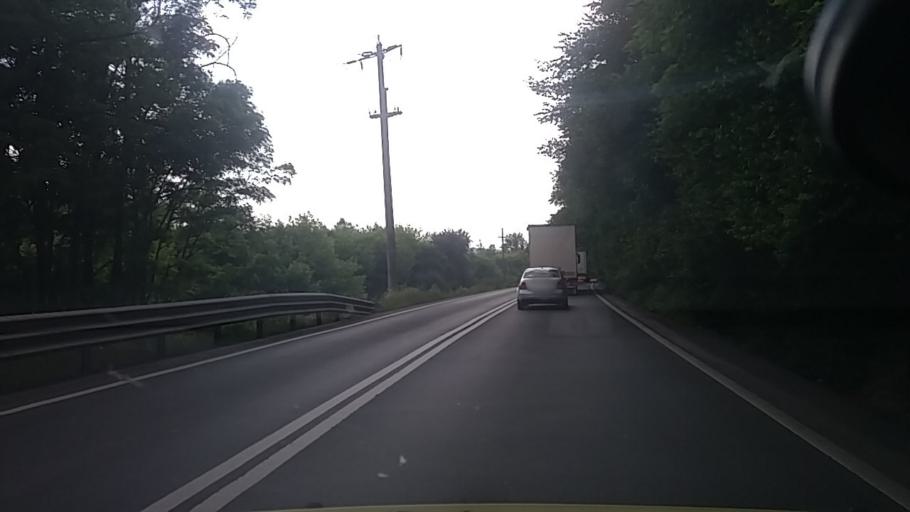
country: RO
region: Arad
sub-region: Comuna Savarsin
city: Savarsin
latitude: 45.9957
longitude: 22.3006
